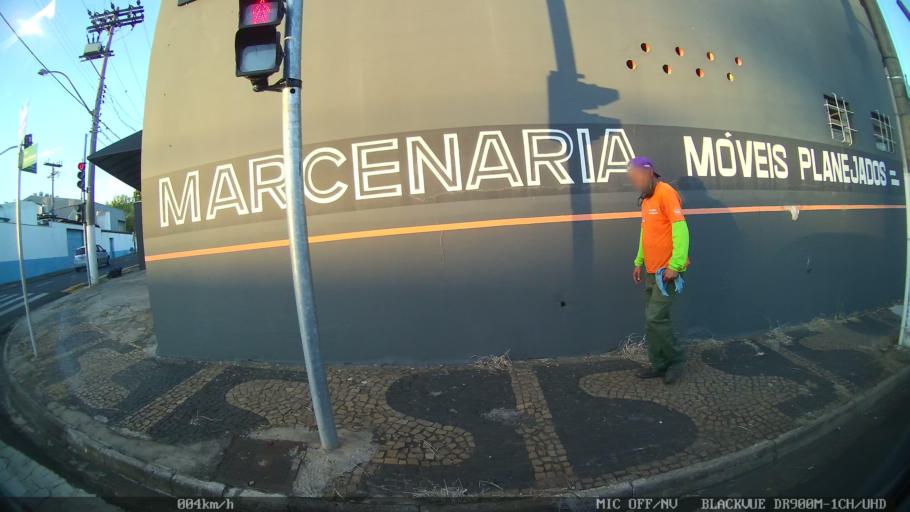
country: BR
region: Sao Paulo
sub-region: Santa Barbara D'Oeste
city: Santa Barbara d'Oeste
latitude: -22.7602
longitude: -47.4164
